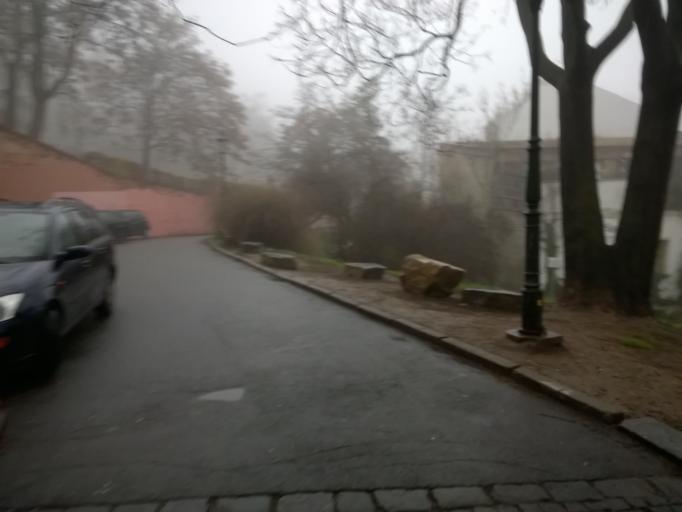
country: CZ
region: South Moravian
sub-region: Mesto Brno
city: Brno
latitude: 49.1919
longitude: 16.6040
